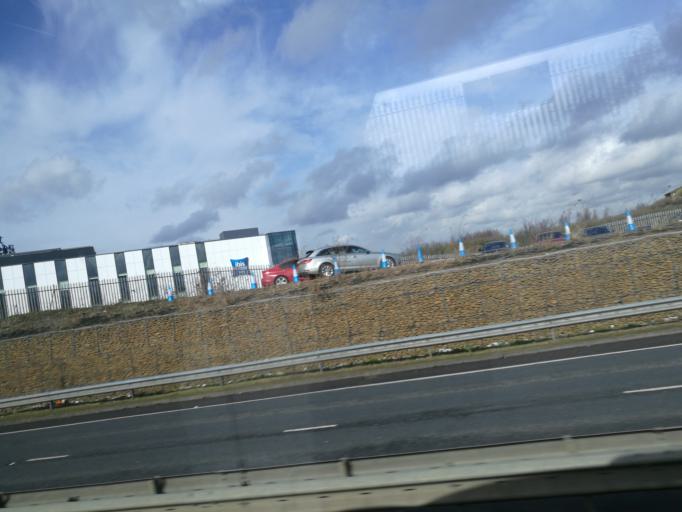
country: GB
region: England
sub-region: Luton
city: Luton
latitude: 51.8749
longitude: -0.3829
